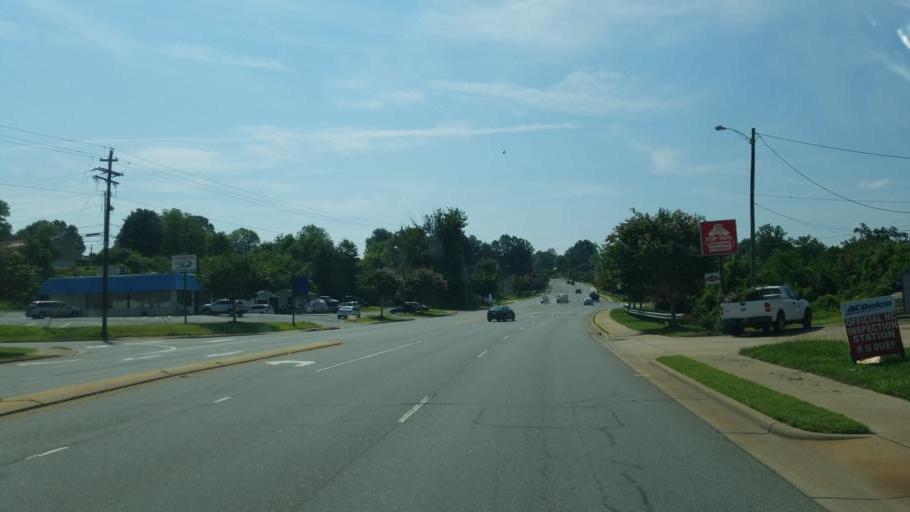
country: US
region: North Carolina
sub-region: Burke County
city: Morganton
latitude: 35.7391
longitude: -81.6793
